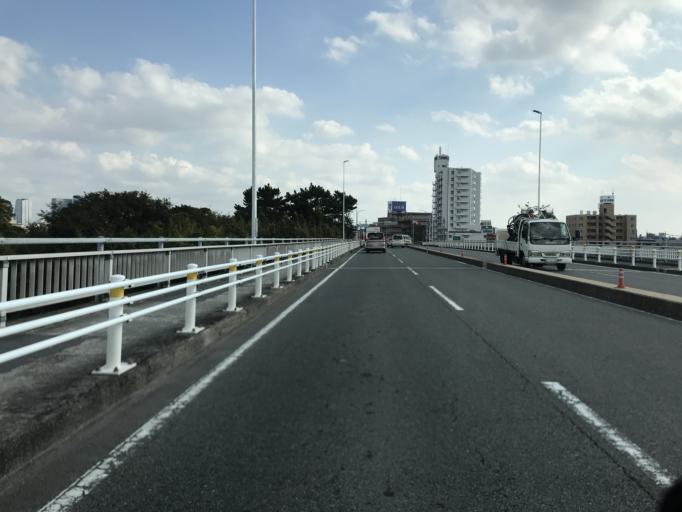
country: JP
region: Aichi
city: Nagoya-shi
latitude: 35.1794
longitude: 136.8463
